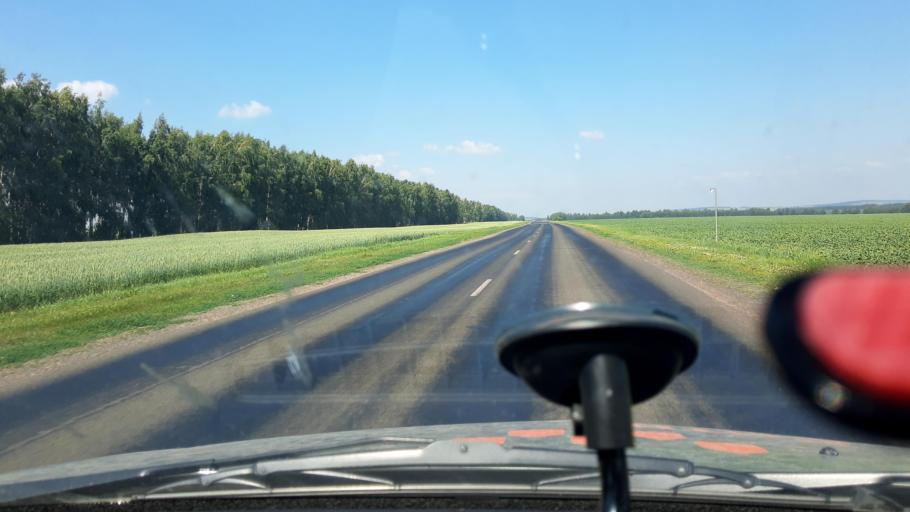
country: RU
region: Bashkortostan
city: Chekmagush
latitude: 55.0885
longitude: 54.6417
